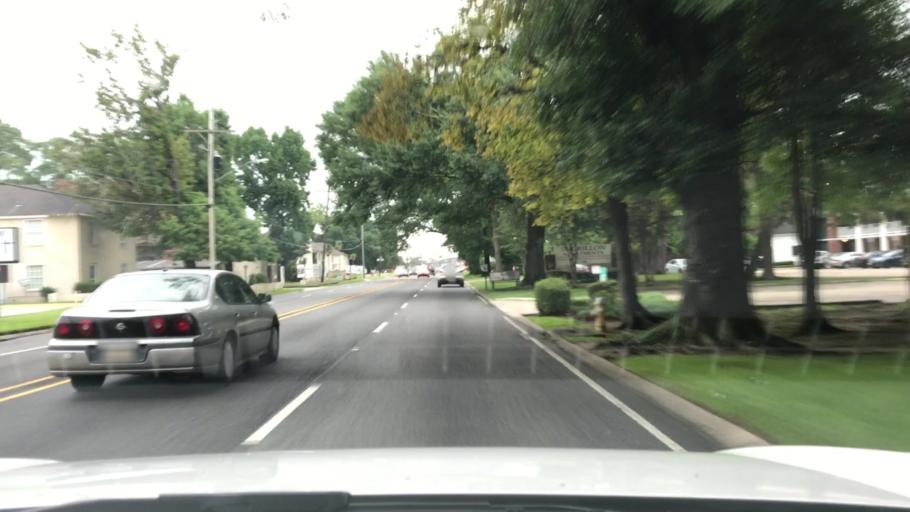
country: US
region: Louisiana
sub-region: East Baton Rouge Parish
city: Baton Rouge
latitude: 30.4588
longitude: -91.1393
